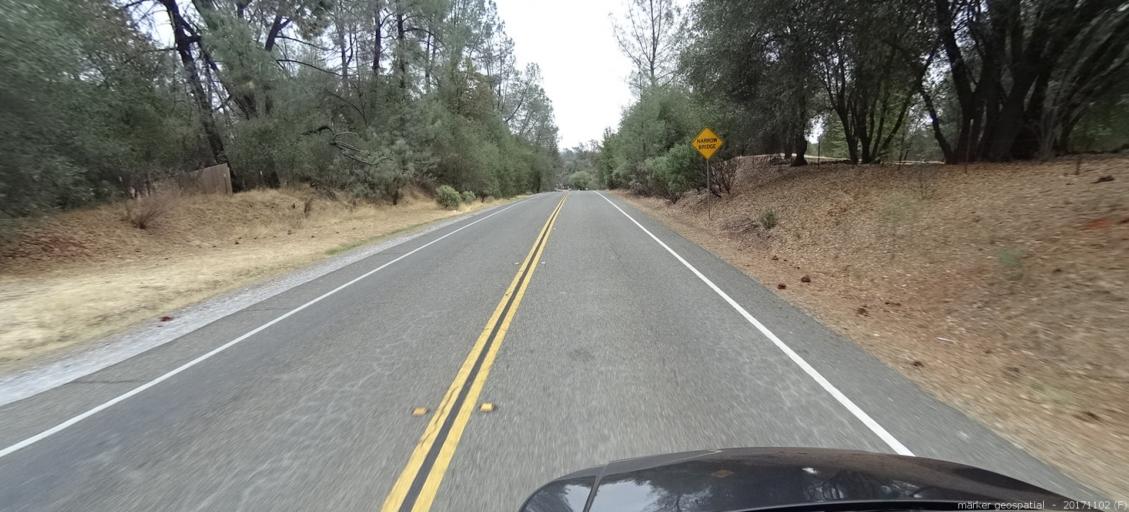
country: US
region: California
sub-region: Shasta County
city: Shasta Lake
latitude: 40.6758
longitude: -122.3056
